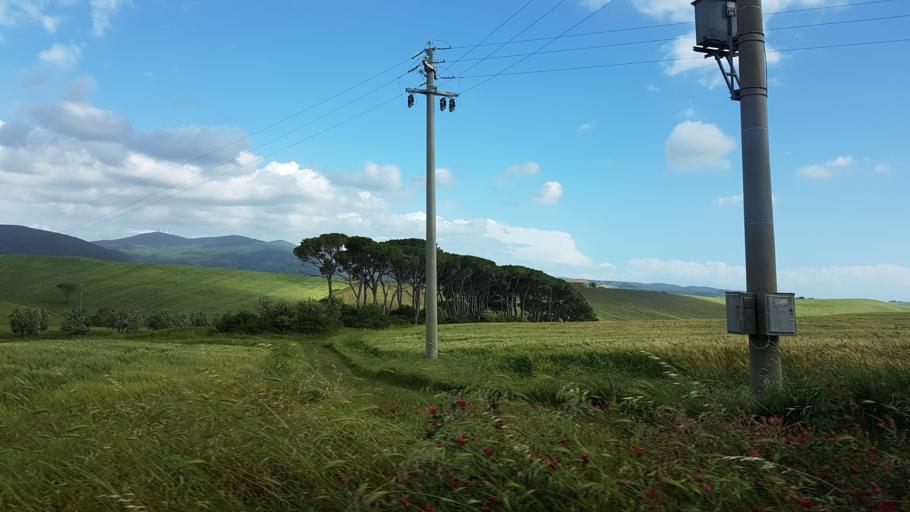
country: IT
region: Tuscany
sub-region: Province of Pisa
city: Santa Luce
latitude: 43.4590
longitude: 10.5289
